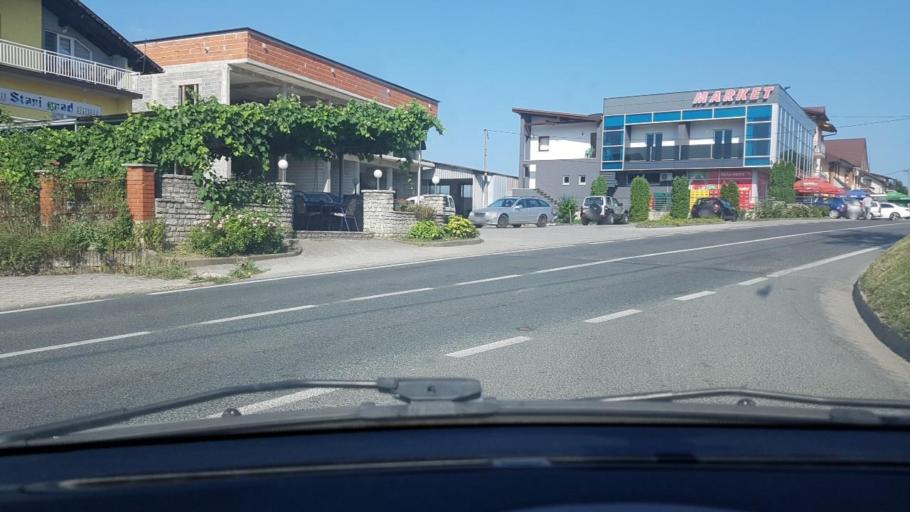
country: BA
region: Federation of Bosnia and Herzegovina
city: Ostrozac
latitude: 44.9072
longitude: 15.9348
